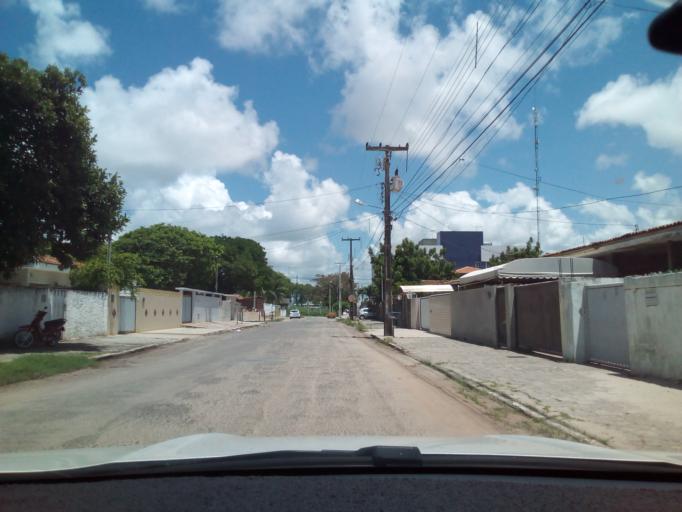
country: BR
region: Paraiba
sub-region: Joao Pessoa
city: Joao Pessoa
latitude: -7.1672
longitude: -34.8700
